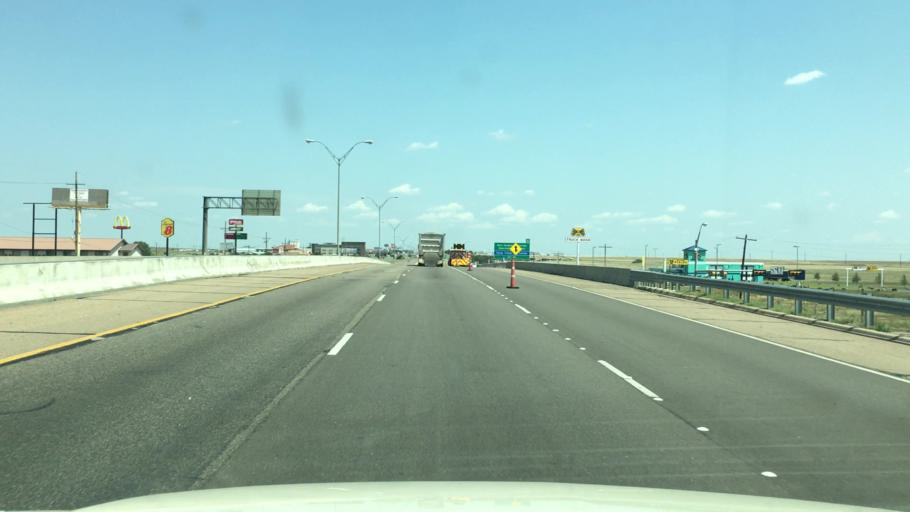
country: US
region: Texas
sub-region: Potter County
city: Amarillo
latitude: 35.1927
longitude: -101.7430
